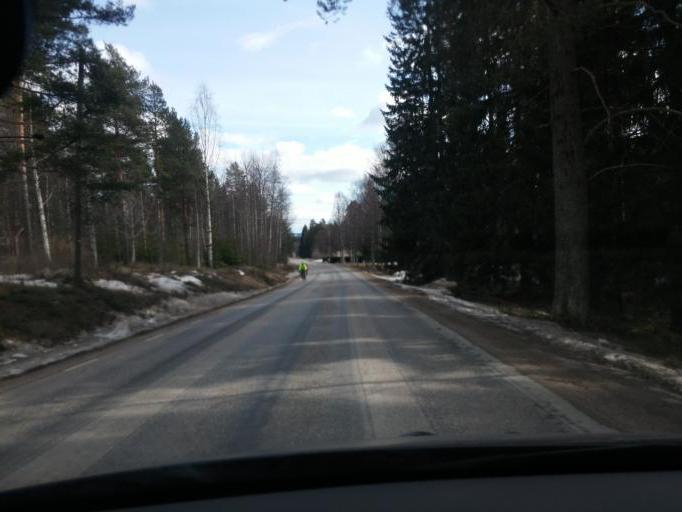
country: SE
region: Gaevleborg
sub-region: Ljusdals Kommun
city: Ljusdal
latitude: 61.8178
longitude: 16.1385
